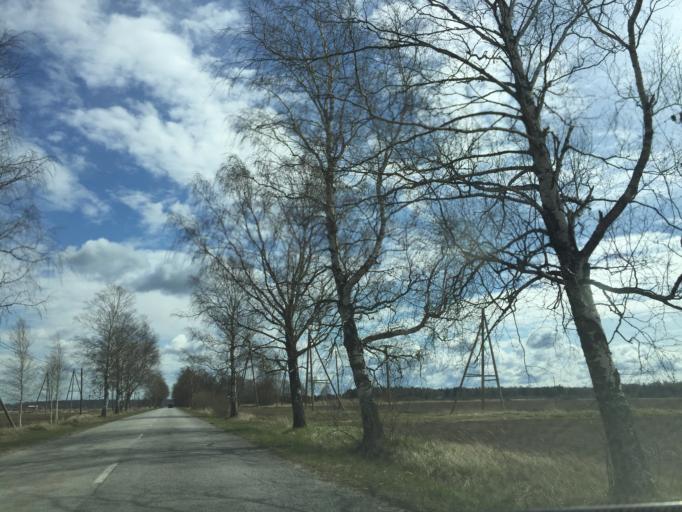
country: LV
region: Salacgrivas
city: Salacgriva
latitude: 57.7472
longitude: 24.3778
